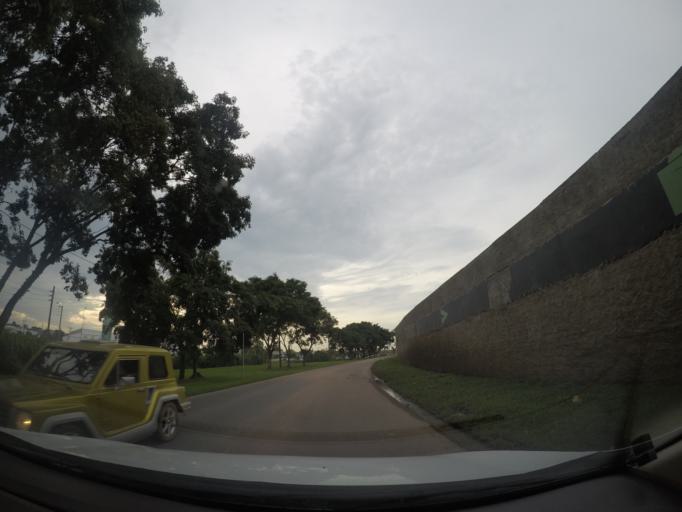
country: BR
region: Parana
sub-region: Curitiba
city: Curitiba
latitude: -25.4649
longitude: -49.2506
